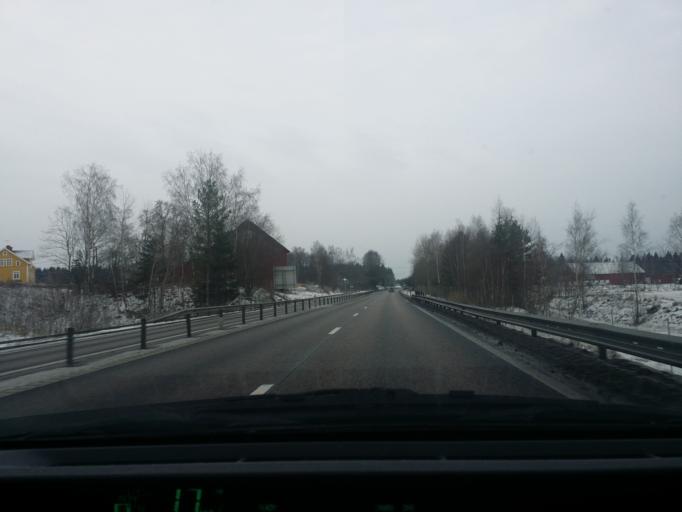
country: SE
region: Vaestra Goetaland
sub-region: Toreboda Kommun
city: Toereboda
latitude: 58.7988
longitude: 14.0503
